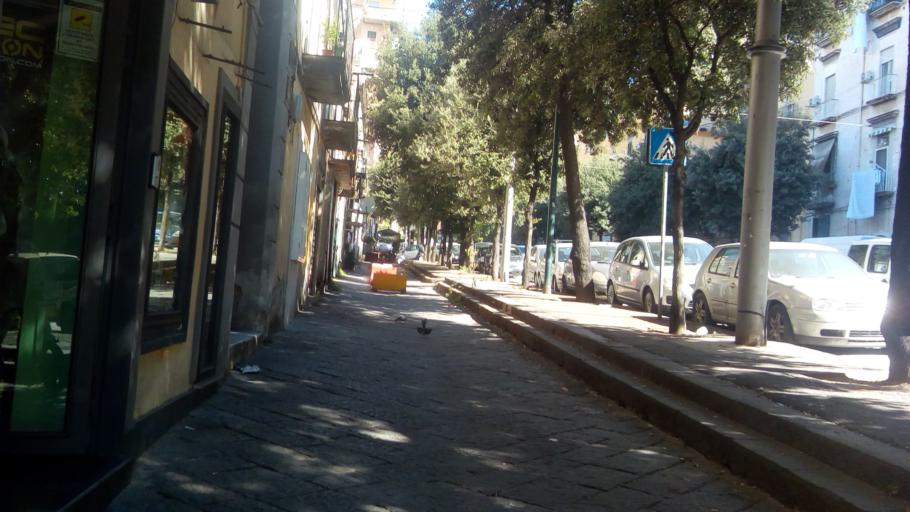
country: IT
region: Campania
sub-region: Provincia di Napoli
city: Napoli
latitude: 40.8624
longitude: 14.2484
